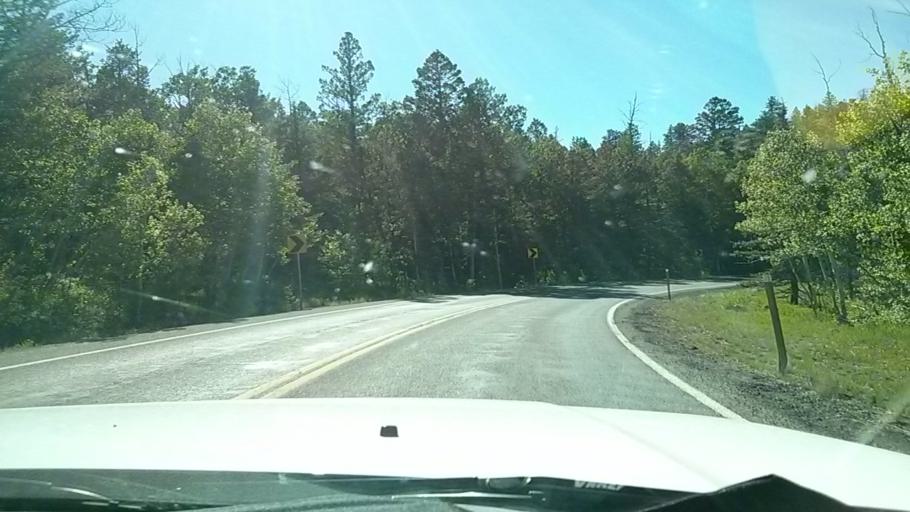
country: US
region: Utah
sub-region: Wayne County
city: Loa
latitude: 38.0868
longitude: -111.3418
